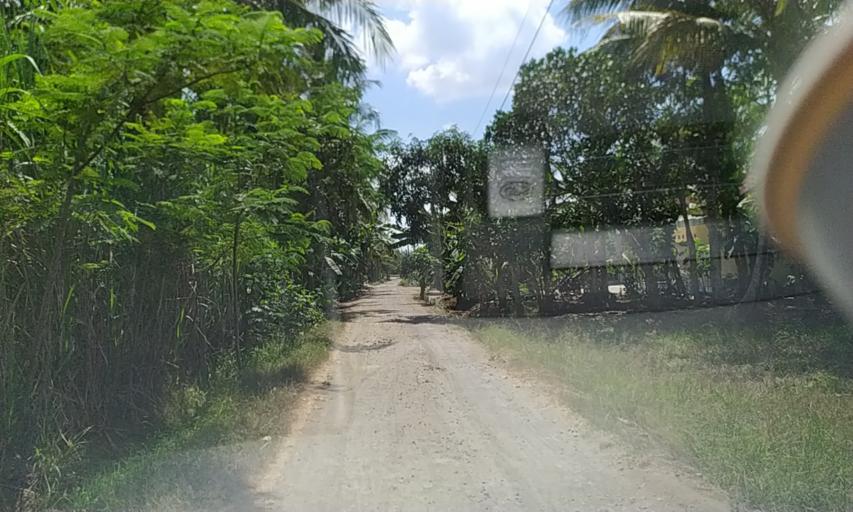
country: ID
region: Central Java
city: Cimrutu
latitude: -7.6112
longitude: 108.7940
